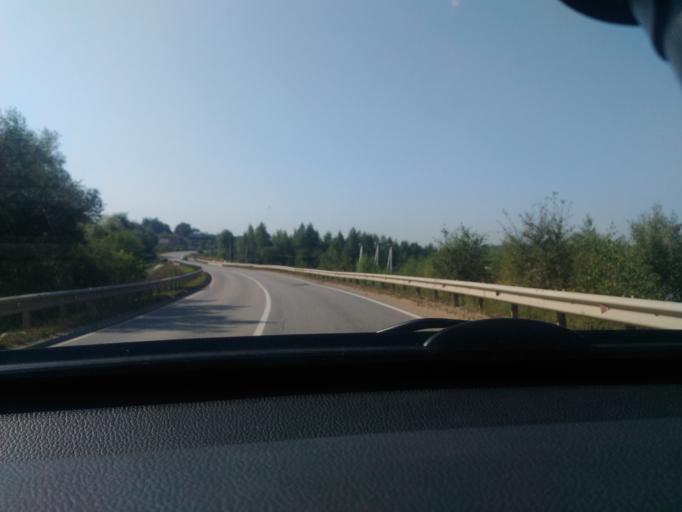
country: RU
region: Moskovskaya
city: Podosinki
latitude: 56.2129
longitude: 37.5430
